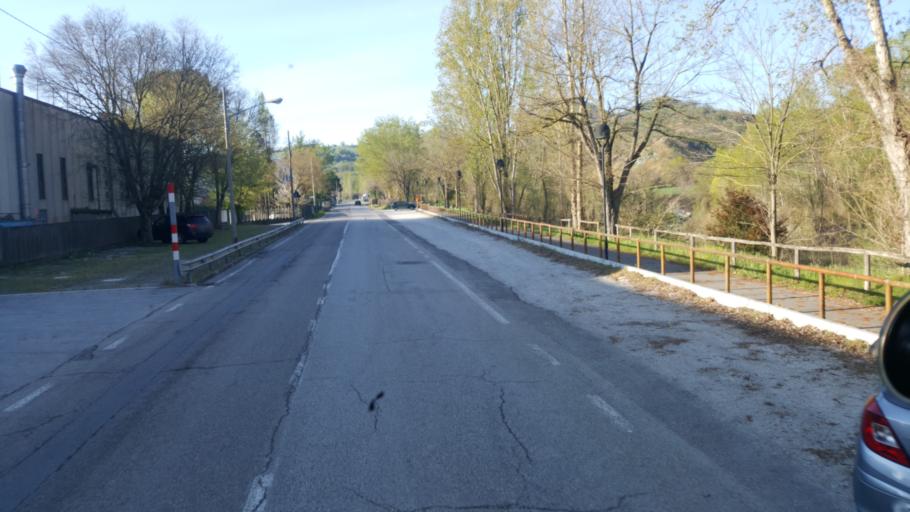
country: SM
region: Acquaviva
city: Acquaviva
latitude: 43.9471
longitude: 12.4054
